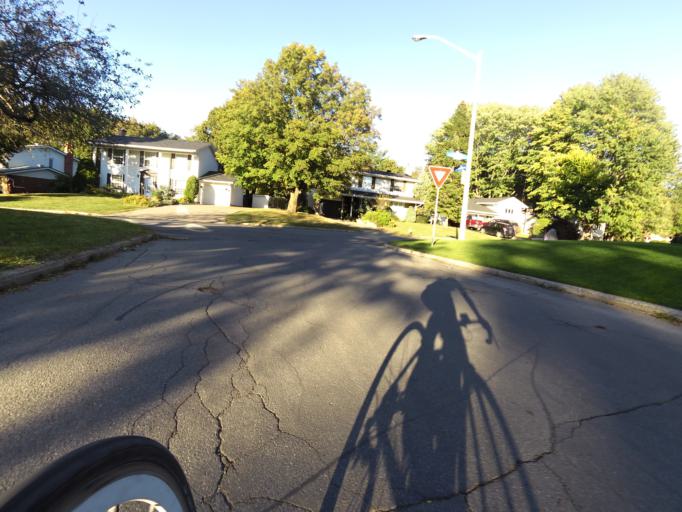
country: CA
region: Ontario
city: Bells Corners
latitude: 45.3354
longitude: -75.7915
